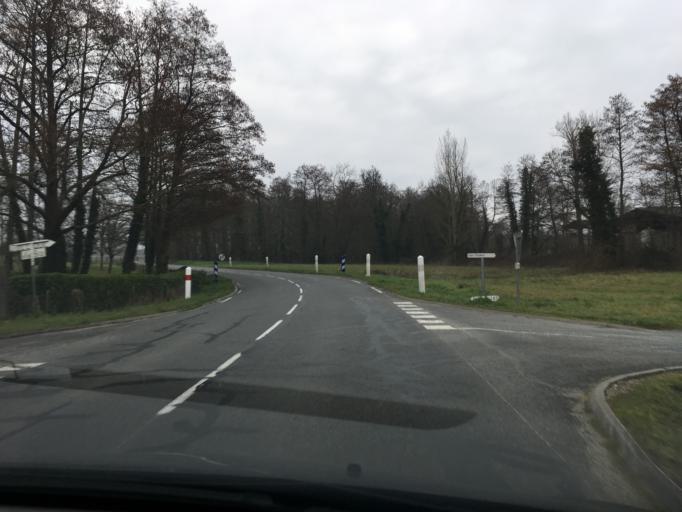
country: FR
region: Aquitaine
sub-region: Departement de la Gironde
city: Saint-Ciers-sur-Gironde
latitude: 45.2711
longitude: -0.5902
